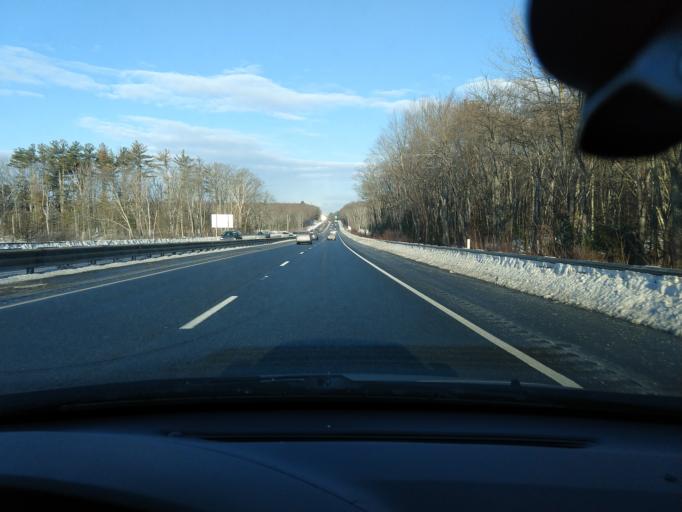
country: US
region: Massachusetts
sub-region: Middlesex County
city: Littleton Common
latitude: 42.5073
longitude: -71.4865
